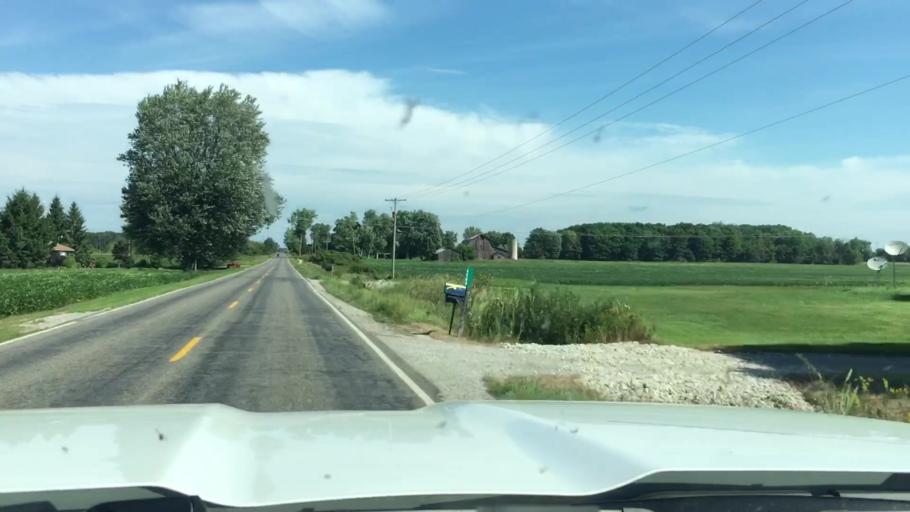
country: US
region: Michigan
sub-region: Saginaw County
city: Hemlock
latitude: 43.4874
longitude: -84.2299
